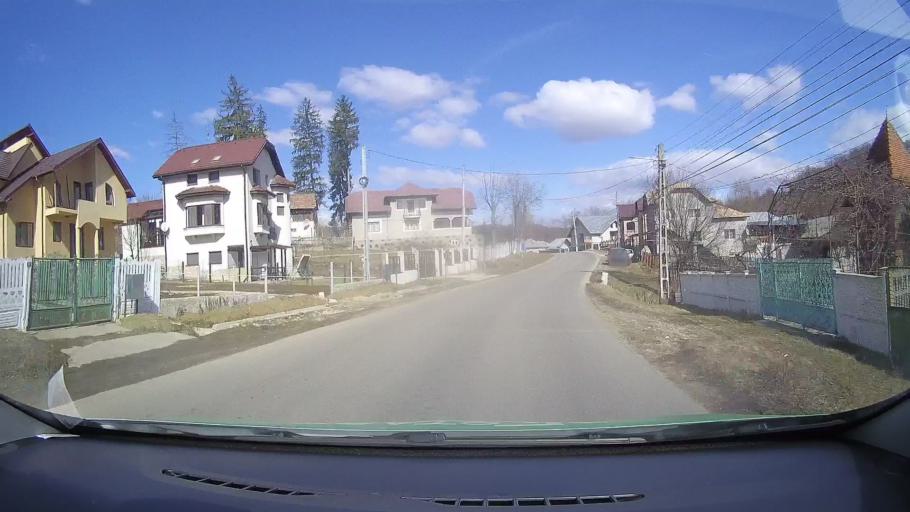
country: RO
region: Dambovita
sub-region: Comuna Vulcana Bai
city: Vulcana Bai
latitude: 45.0682
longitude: 25.3784
